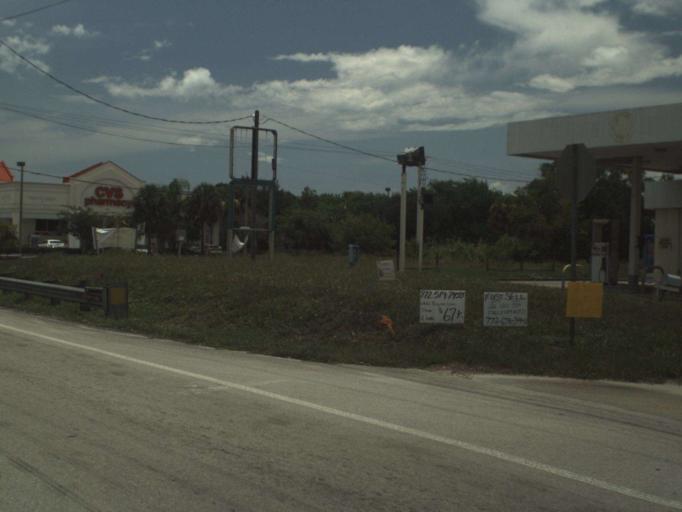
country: US
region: Florida
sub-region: Saint Lucie County
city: Lakewood Park
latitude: 27.5210
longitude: -80.3991
